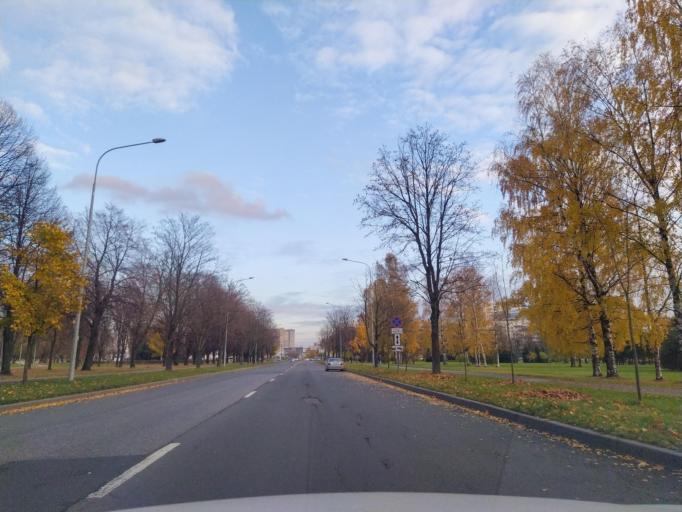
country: RU
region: Leningrad
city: Kalininskiy
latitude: 59.9815
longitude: 30.4156
